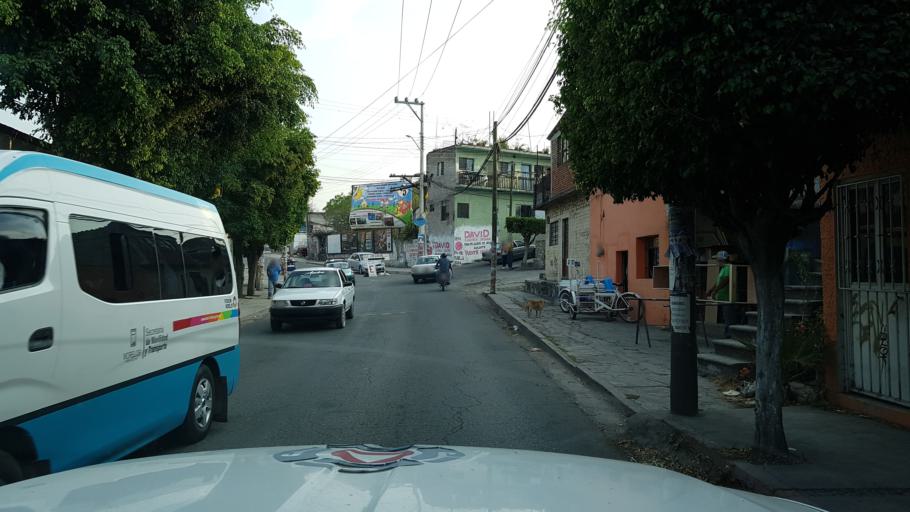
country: MX
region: Morelos
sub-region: Ayala
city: Ciudad Ayala
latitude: 18.7702
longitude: -98.9835
